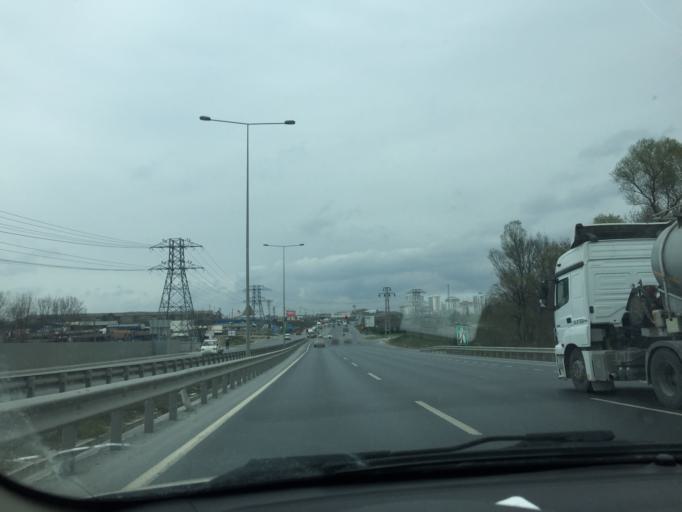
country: TR
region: Istanbul
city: Basaksehir
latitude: 41.1363
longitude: 28.8136
